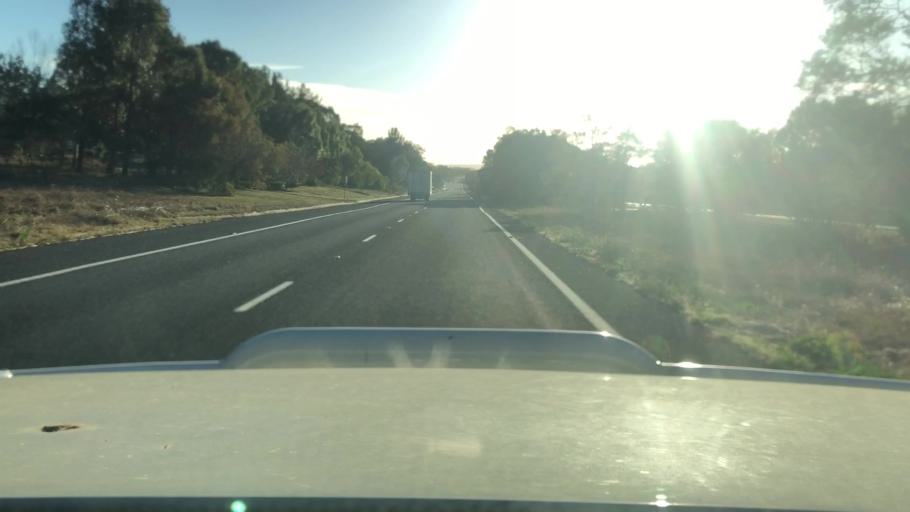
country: AU
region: New South Wales
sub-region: Wingecarribee
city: Bundanoon
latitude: -34.6149
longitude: 150.2177
